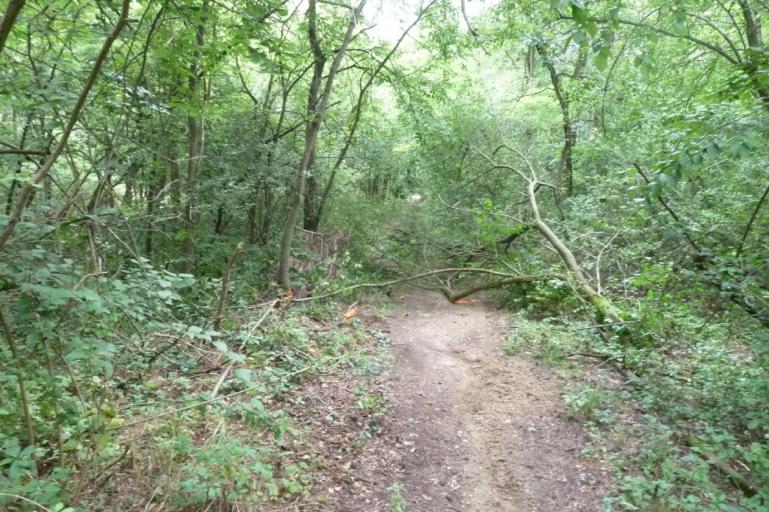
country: HU
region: Pest
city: Godollo
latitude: 47.6284
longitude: 19.3499
